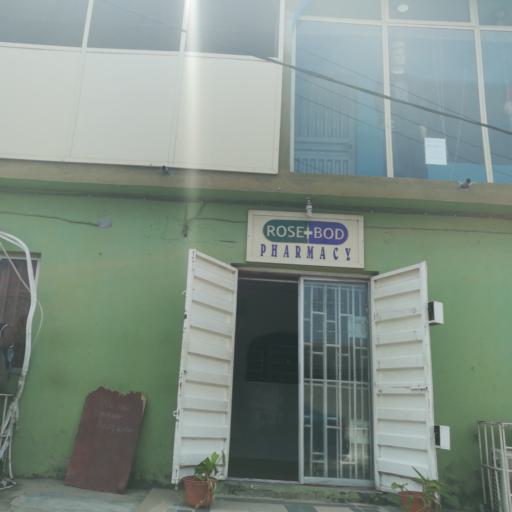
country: NG
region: Lagos
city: Ojota
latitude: 6.5749
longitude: 3.4014
